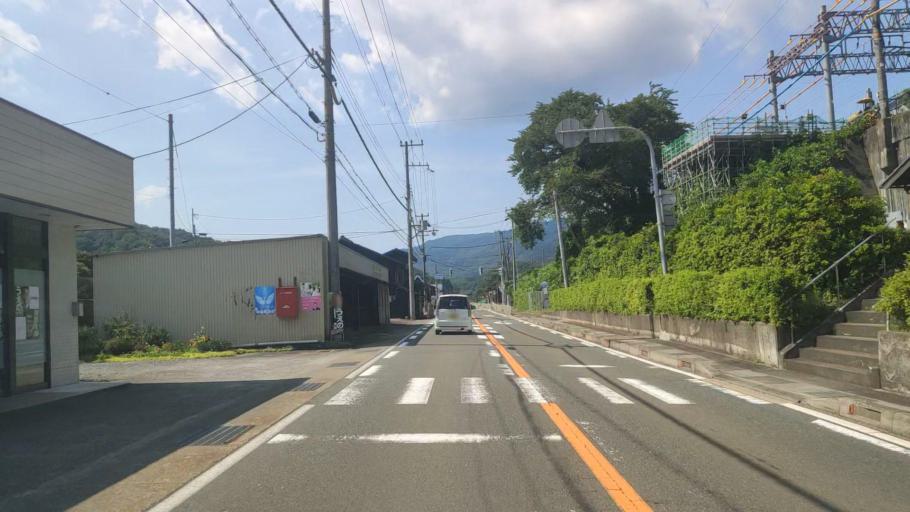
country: JP
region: Fukui
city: Tsuruga
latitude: 35.5382
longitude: 136.1513
